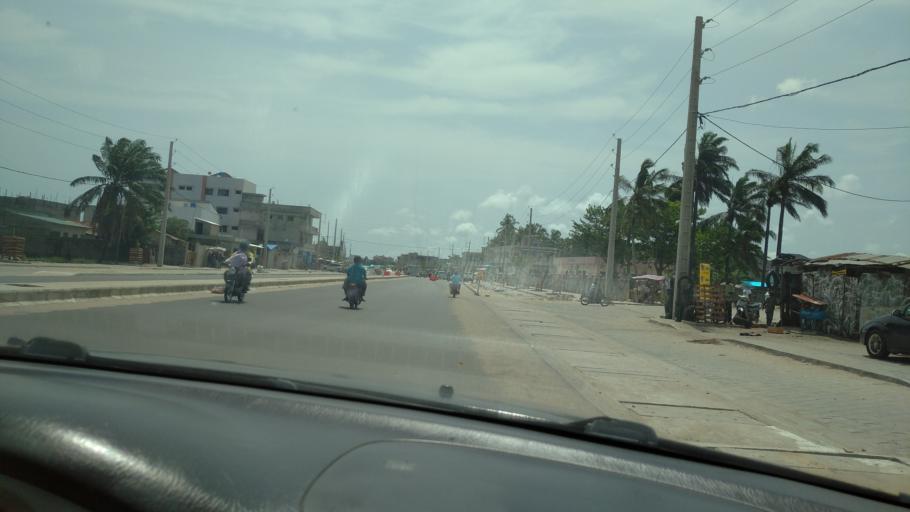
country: BJ
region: Littoral
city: Cotonou
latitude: 6.3744
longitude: 2.4953
